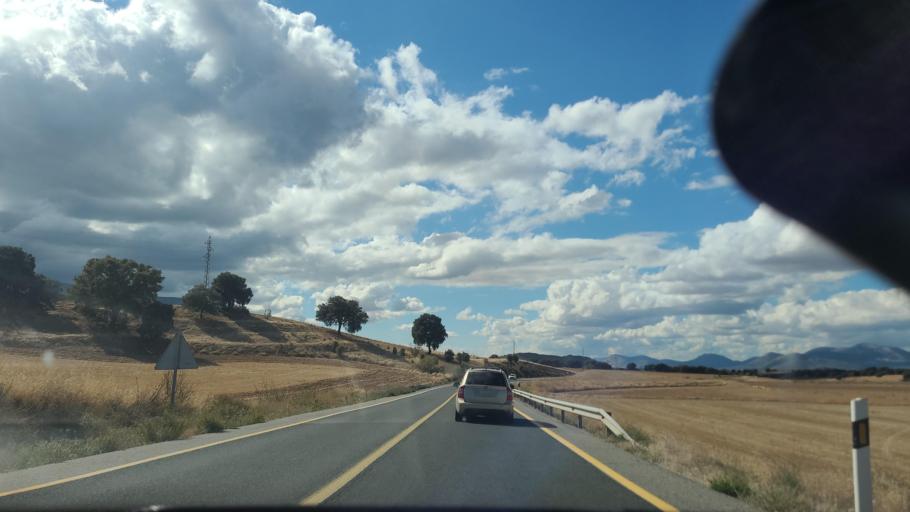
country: ES
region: Andalusia
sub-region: Provincia de Granada
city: Pinar
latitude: 37.3971
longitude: -3.4284
